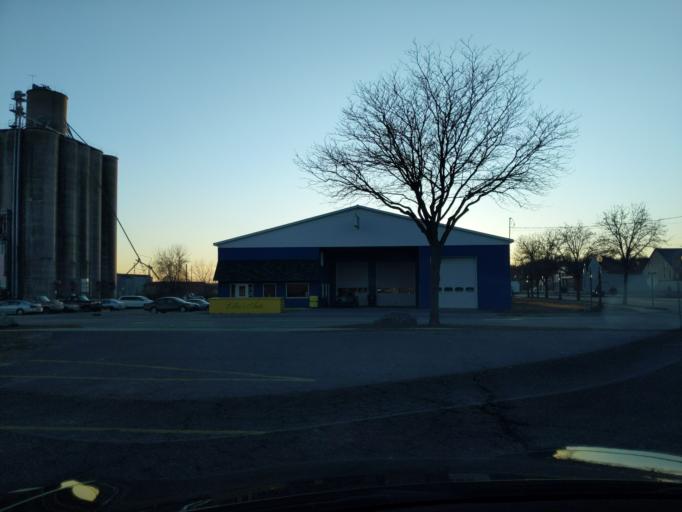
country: US
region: Michigan
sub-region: Ionia County
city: Ionia
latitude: 42.9813
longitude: -85.0673
